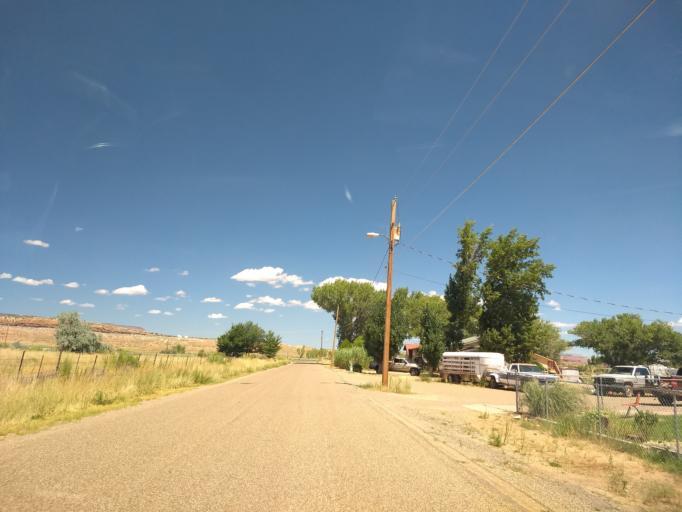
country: US
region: Arizona
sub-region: Coconino County
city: Fredonia
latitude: 36.9438
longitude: -112.5354
